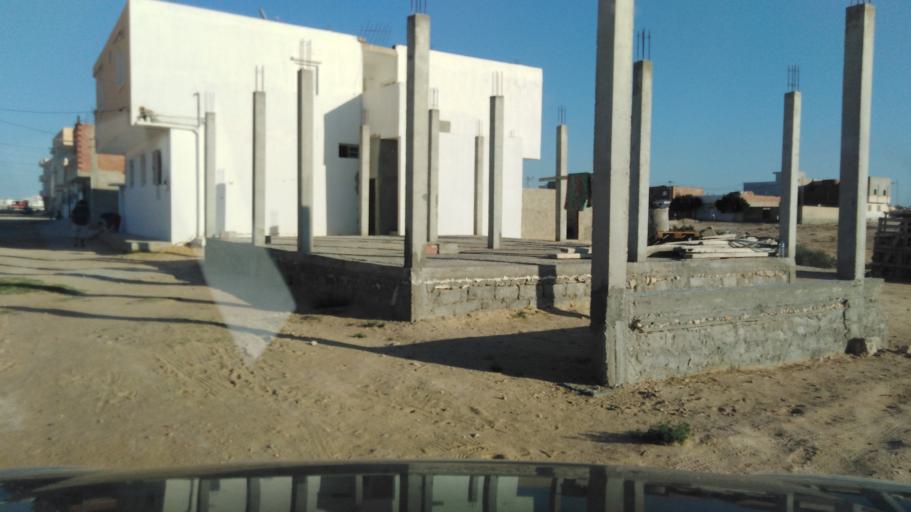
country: TN
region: Qabis
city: Gabes
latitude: 33.9548
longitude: 10.0075
